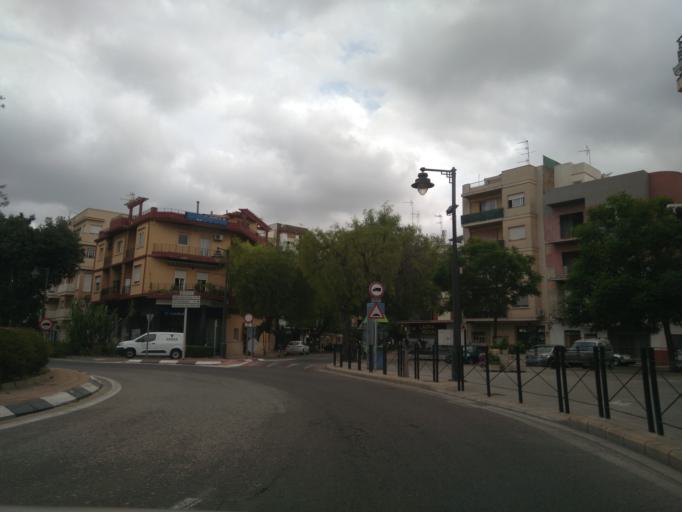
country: ES
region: Valencia
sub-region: Provincia de Valencia
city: L'Alcudia
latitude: 39.1992
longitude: -0.5048
